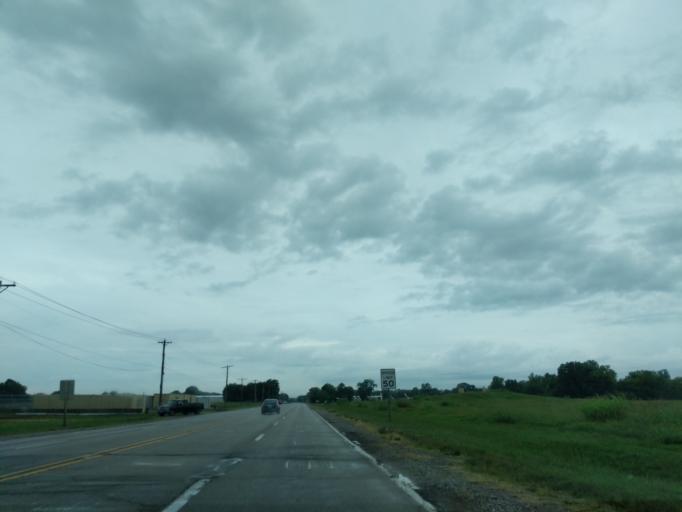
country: US
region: Illinois
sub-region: Saint Clair County
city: Fairmont City
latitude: 38.6590
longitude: -90.0710
